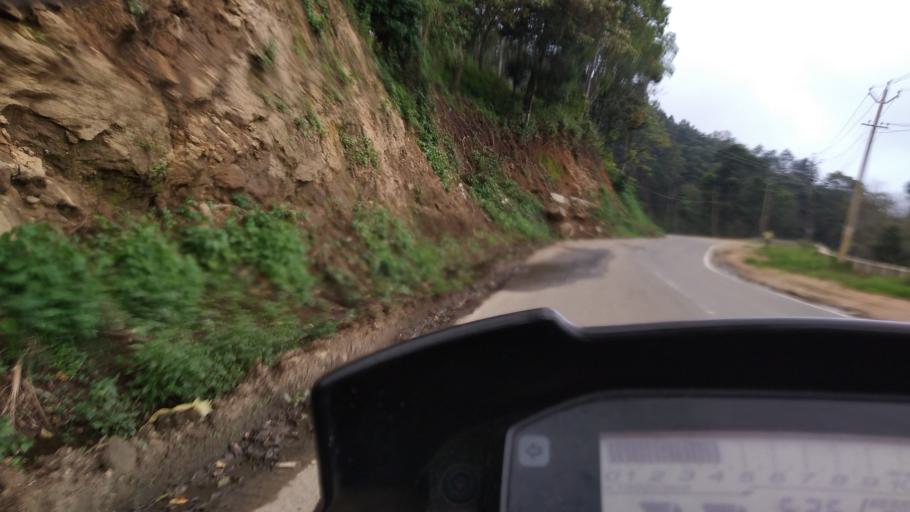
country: IN
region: Tamil Nadu
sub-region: Theni
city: Bodinayakkanur
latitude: 10.0051
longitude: 77.2269
